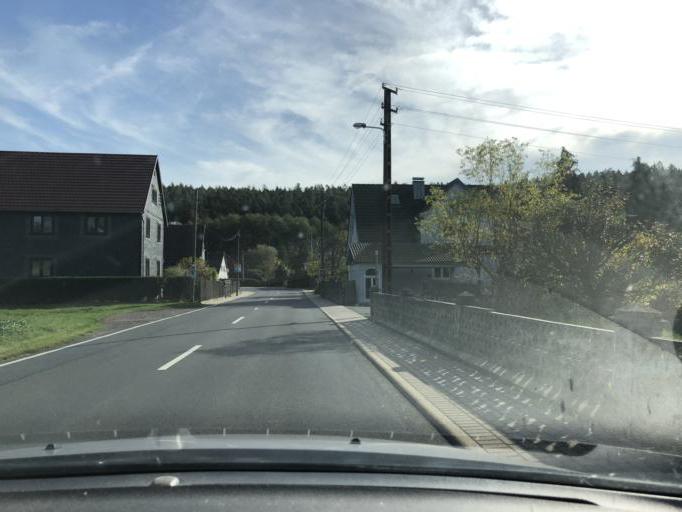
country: DE
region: Thuringia
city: Schleusingen
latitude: 50.4866
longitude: 10.8045
